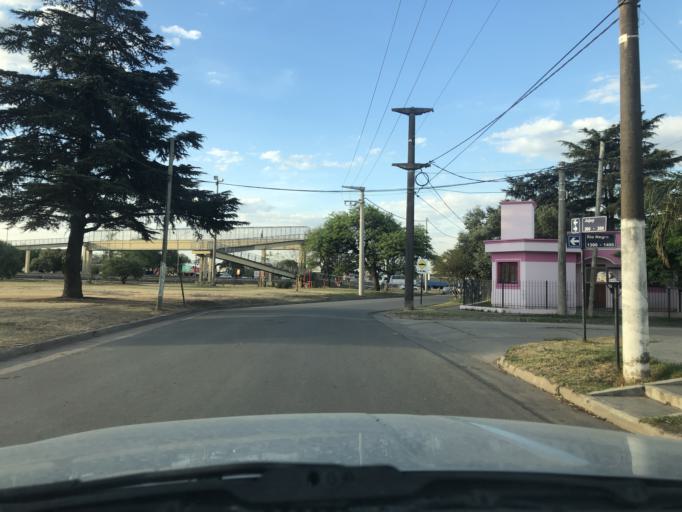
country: AR
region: Cordoba
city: Jesus Maria
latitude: -30.9799
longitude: -64.0851
